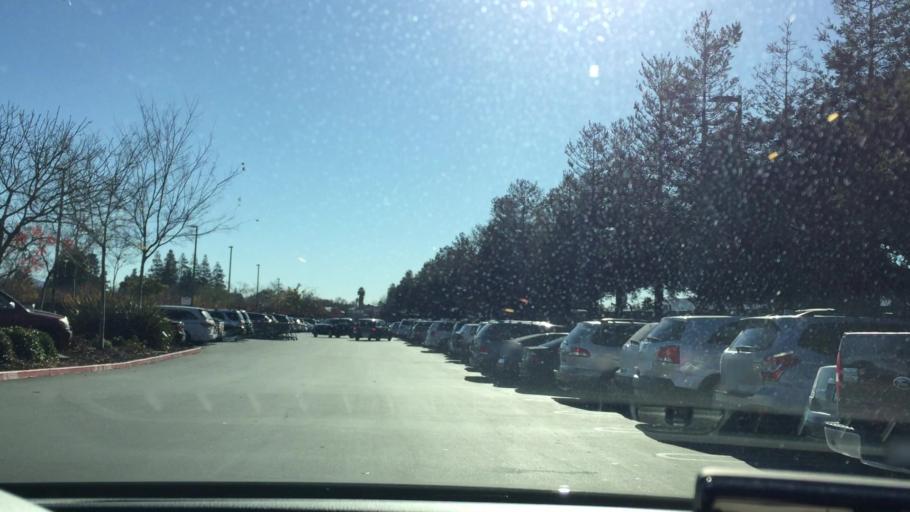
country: US
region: California
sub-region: Santa Clara County
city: Milpitas
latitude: 37.3903
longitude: -121.8855
